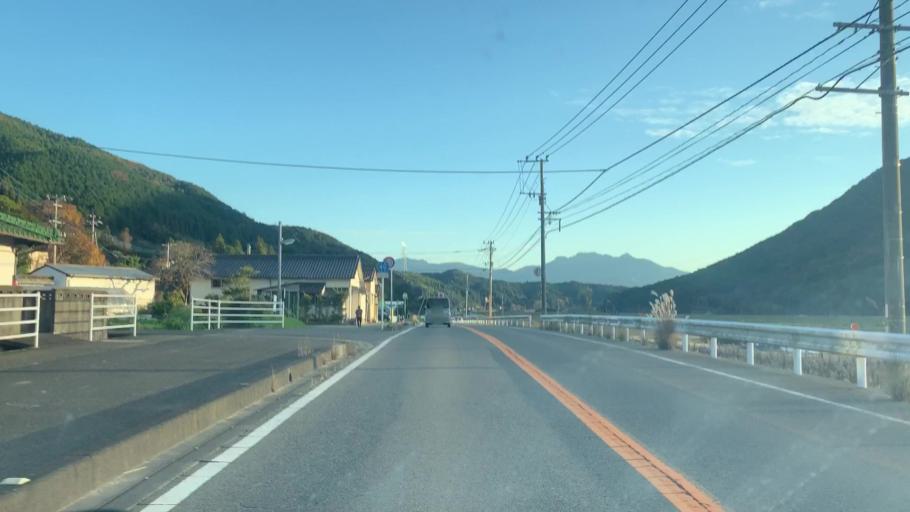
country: JP
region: Saga Prefecture
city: Karatsu
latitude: 33.3720
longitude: 130.0028
